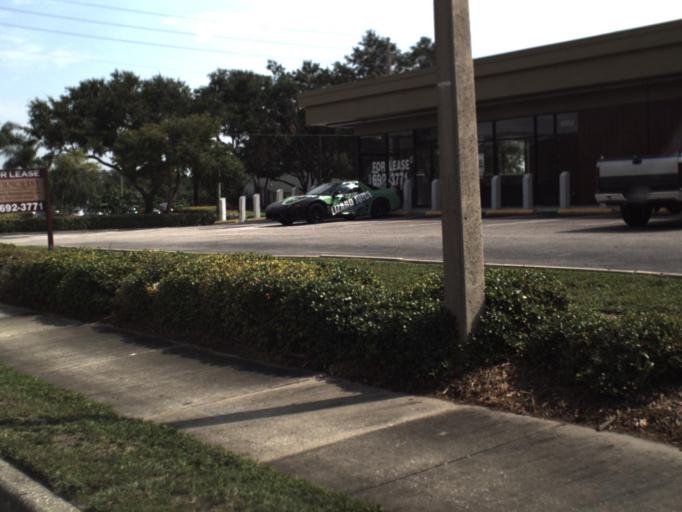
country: US
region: Florida
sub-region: Pinellas County
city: Gandy
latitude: 27.8569
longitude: -82.6387
